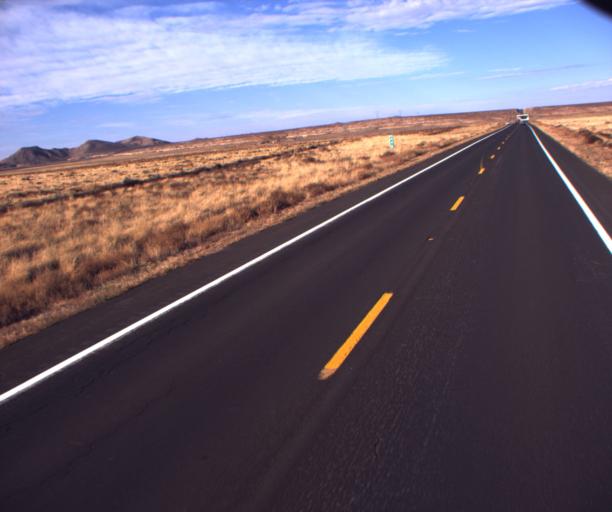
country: US
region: Arizona
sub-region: Apache County
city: Lukachukai
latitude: 36.9622
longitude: -109.4232
